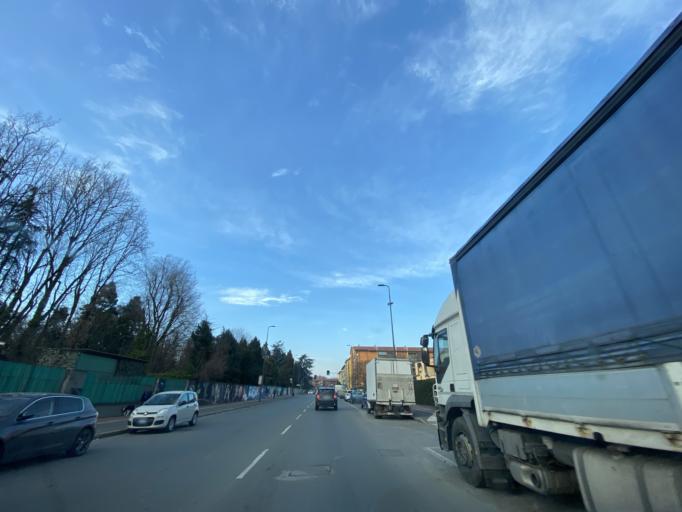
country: IT
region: Lombardy
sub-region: Citta metropolitana di Milano
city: Novate Milanese
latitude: 45.5157
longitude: 9.1361
